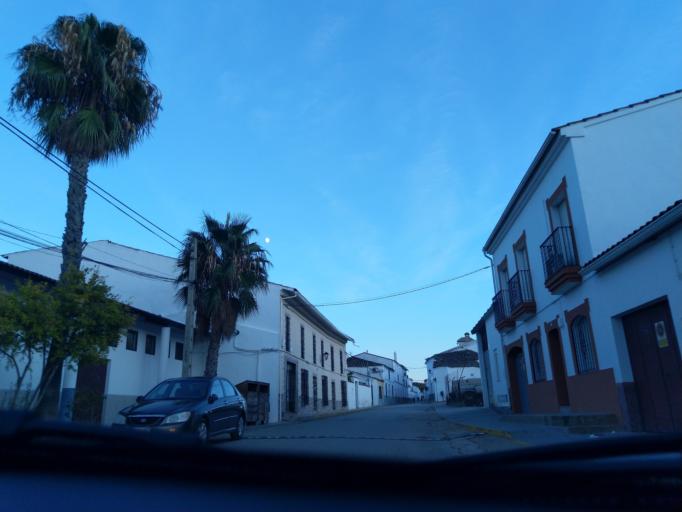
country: ES
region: Extremadura
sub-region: Provincia de Badajoz
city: Reina
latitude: 38.1542
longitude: -5.8991
